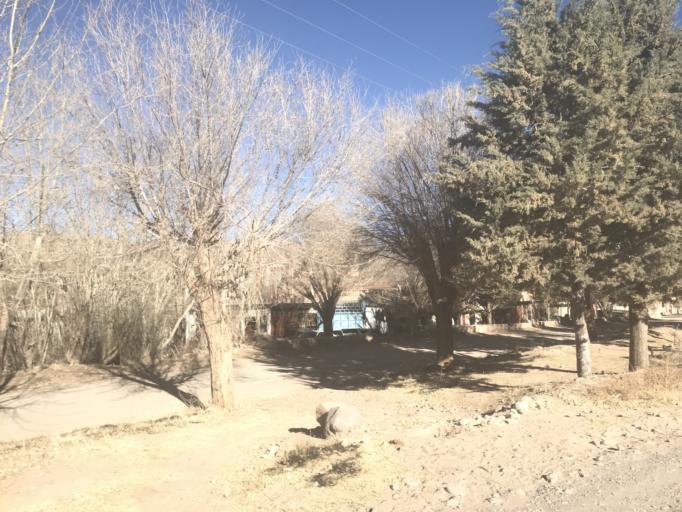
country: AR
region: Jujuy
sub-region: Departamento de Humahuaca
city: Humahuaca
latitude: -23.2129
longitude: -65.3472
